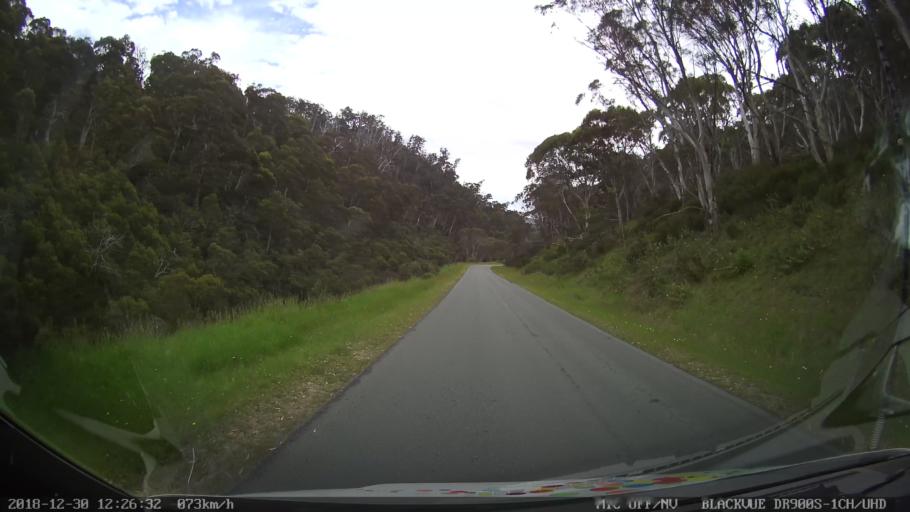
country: AU
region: New South Wales
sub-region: Snowy River
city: Jindabyne
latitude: -36.3380
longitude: 148.4894
